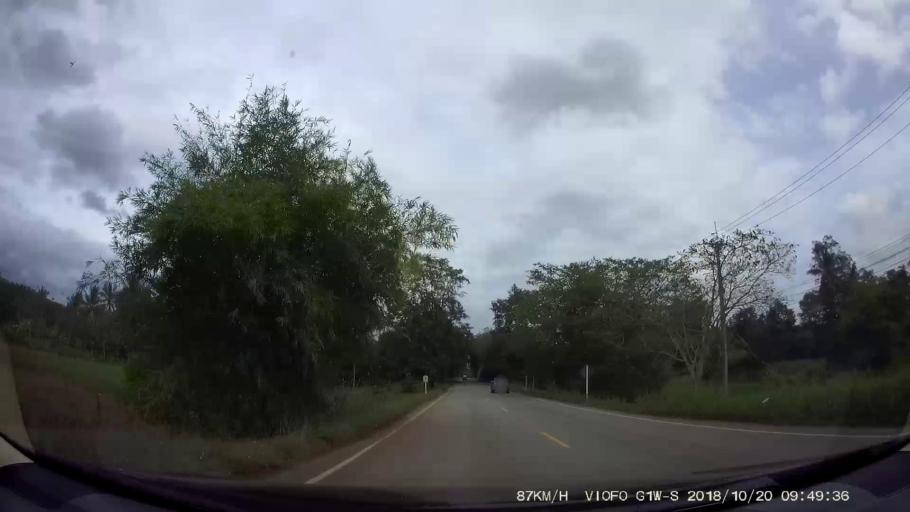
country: TH
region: Chaiyaphum
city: Khon San
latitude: 16.5215
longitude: 101.9046
